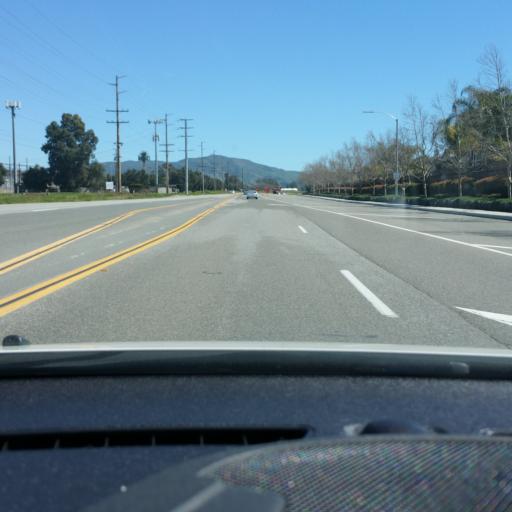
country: US
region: California
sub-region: Riverside County
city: Temecula
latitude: 33.4893
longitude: -117.0663
